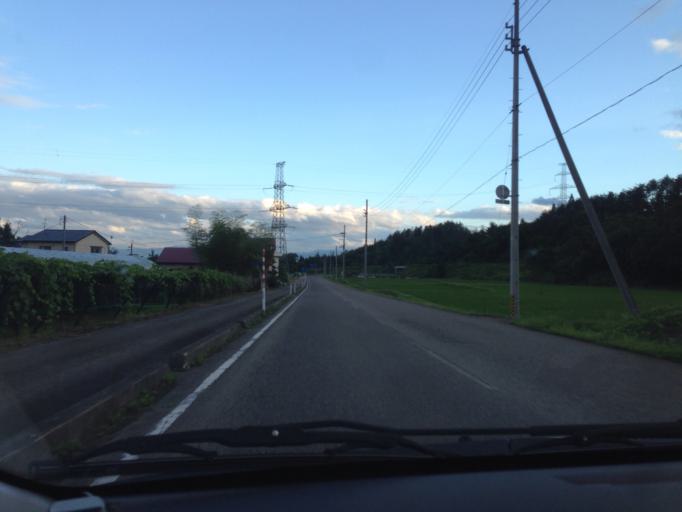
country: JP
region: Fukushima
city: Kitakata
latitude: 37.7128
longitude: 139.8698
